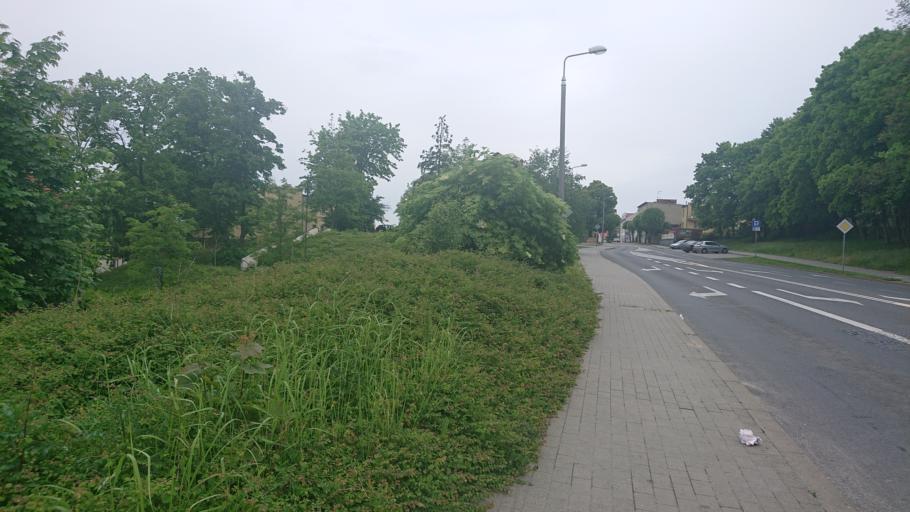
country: PL
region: Pomeranian Voivodeship
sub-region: Powiat chojnicki
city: Chojnice
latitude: 53.6945
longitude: 17.5667
